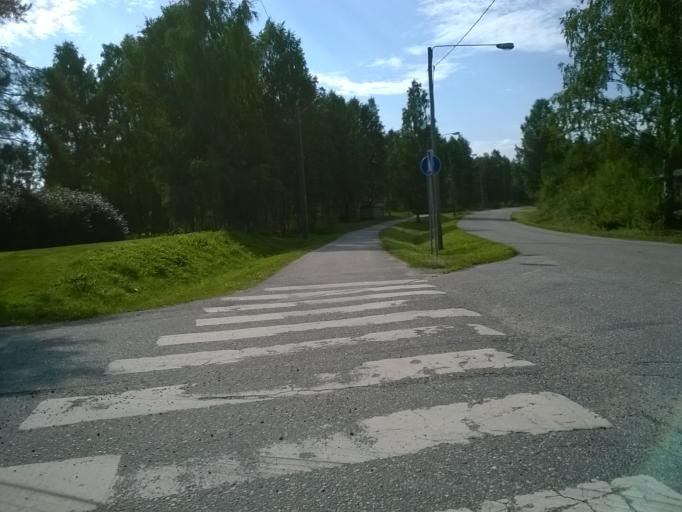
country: FI
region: Kainuu
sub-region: Kehys-Kainuu
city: Kuhmo
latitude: 64.1286
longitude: 29.4709
